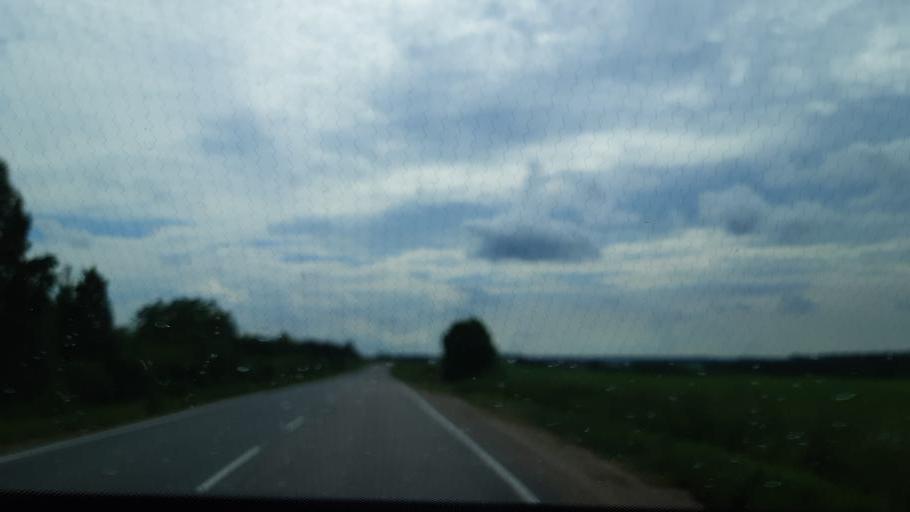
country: RU
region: Moskovskaya
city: Vereya
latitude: 55.2134
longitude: 36.0037
